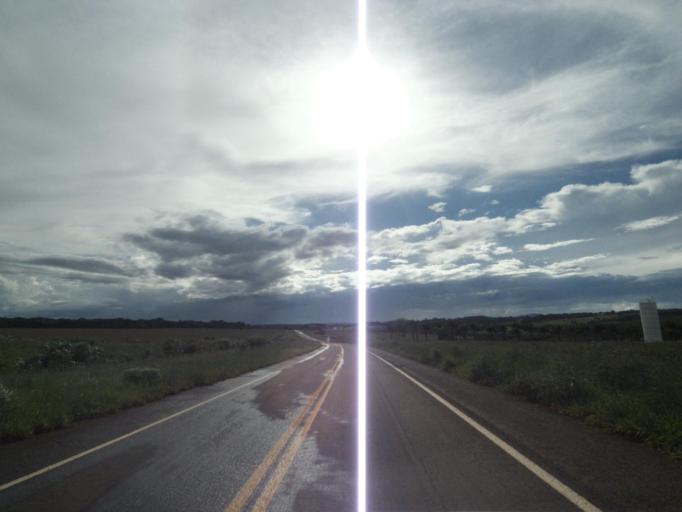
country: BR
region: Goias
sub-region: Jaragua
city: Jaragua
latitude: -15.9020
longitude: -49.5369
